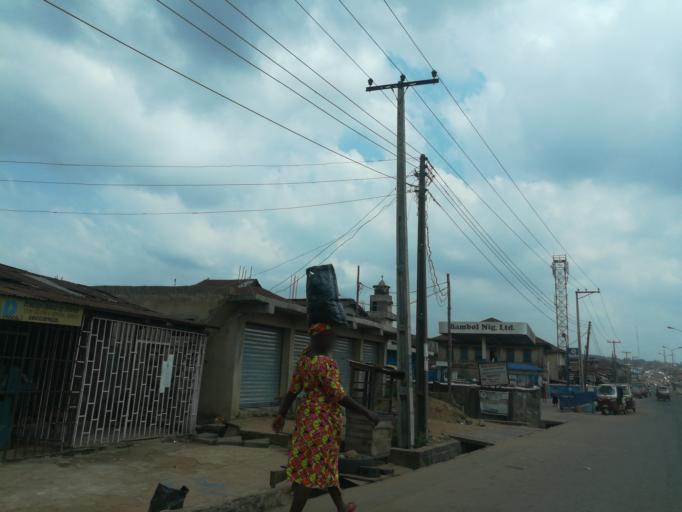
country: NG
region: Oyo
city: Ibadan
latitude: 7.3836
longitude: 3.9024
